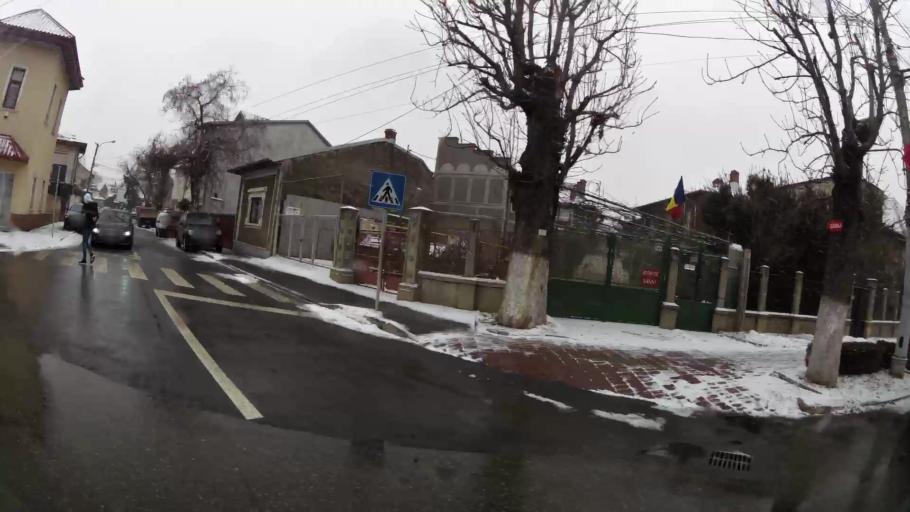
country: RO
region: Dambovita
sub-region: Municipiul Targoviste
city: Targoviste
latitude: 44.9218
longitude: 25.4570
